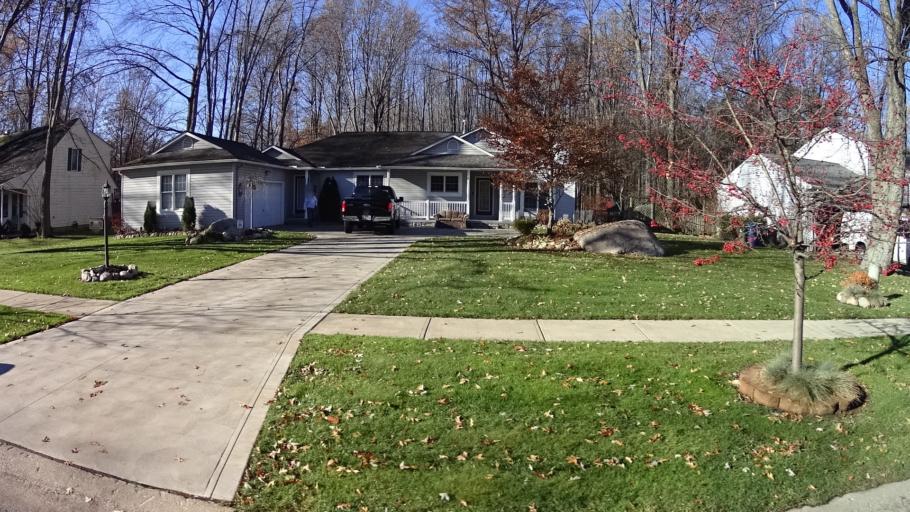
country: US
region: Ohio
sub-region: Lorain County
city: North Ridgeville
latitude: 41.4136
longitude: -81.9961
